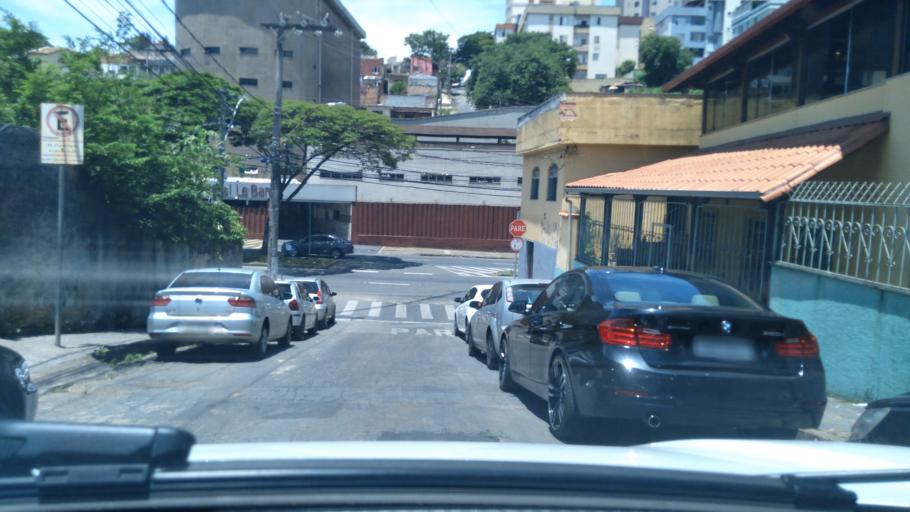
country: BR
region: Minas Gerais
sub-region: Contagem
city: Contagem
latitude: -19.9284
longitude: -43.9957
